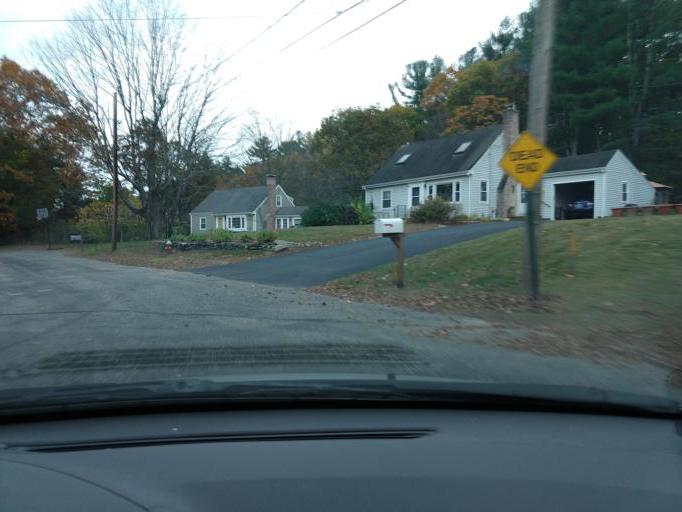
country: US
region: Massachusetts
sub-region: Middlesex County
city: Concord
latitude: 42.4644
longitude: -71.3342
